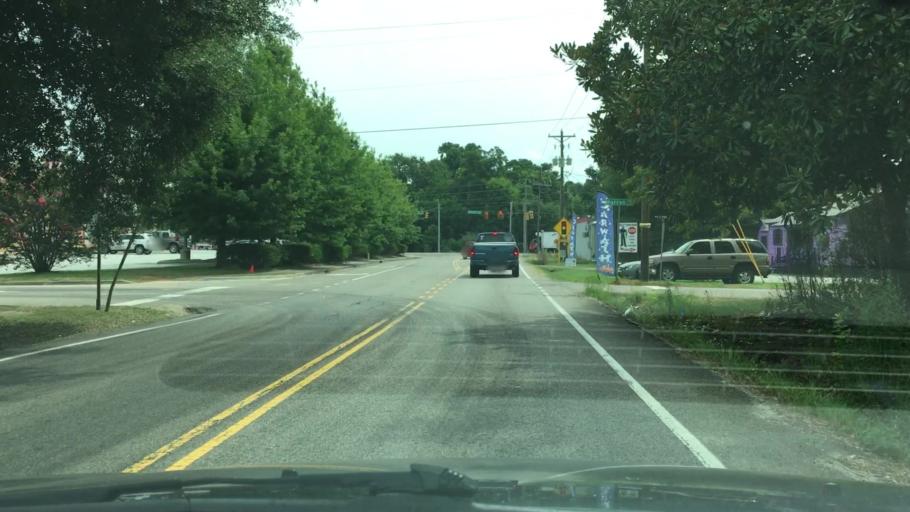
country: US
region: South Carolina
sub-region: Aiken County
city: Aiken
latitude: 33.5142
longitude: -81.7162
